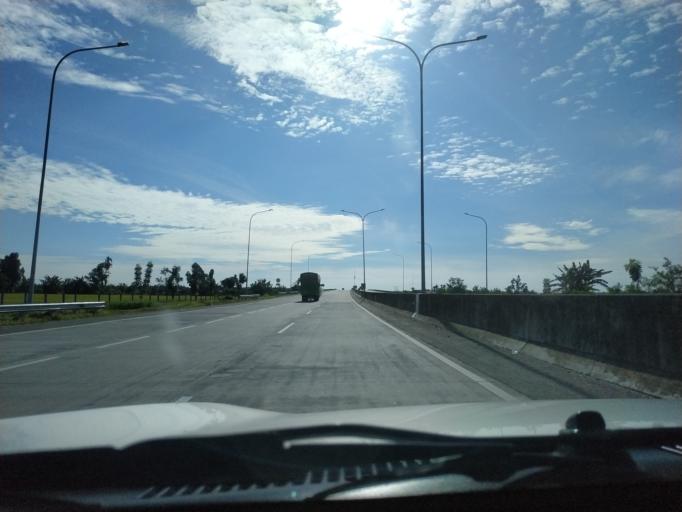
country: ID
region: North Sumatra
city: Percut
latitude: 3.5360
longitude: 98.8590
